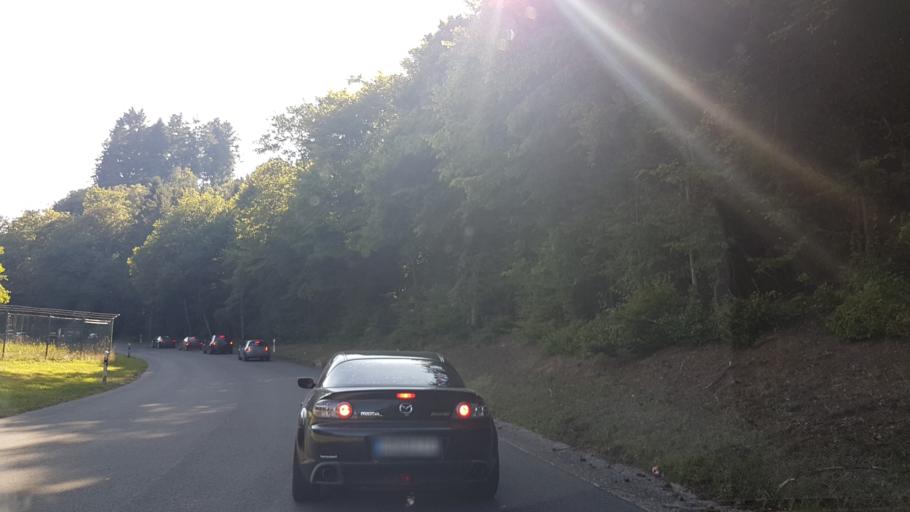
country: DE
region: Rheinland-Pfalz
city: Ruschberg
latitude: 49.6229
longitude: 7.3067
